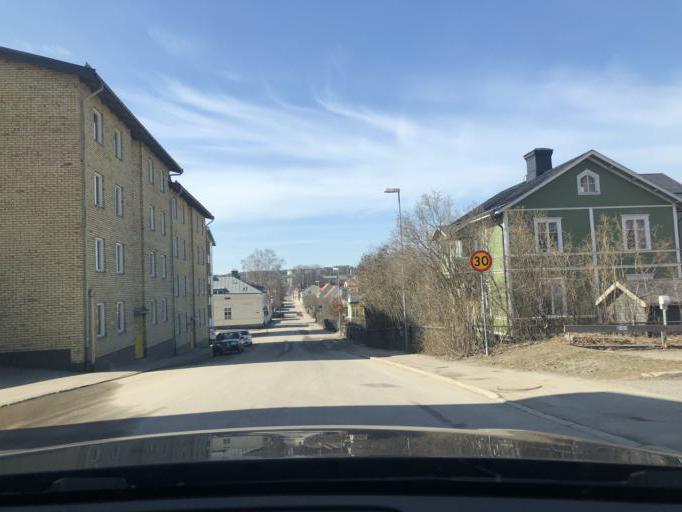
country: SE
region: Gaevleborg
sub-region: Hudiksvalls Kommun
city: Hudiksvall
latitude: 61.7286
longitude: 17.1218
